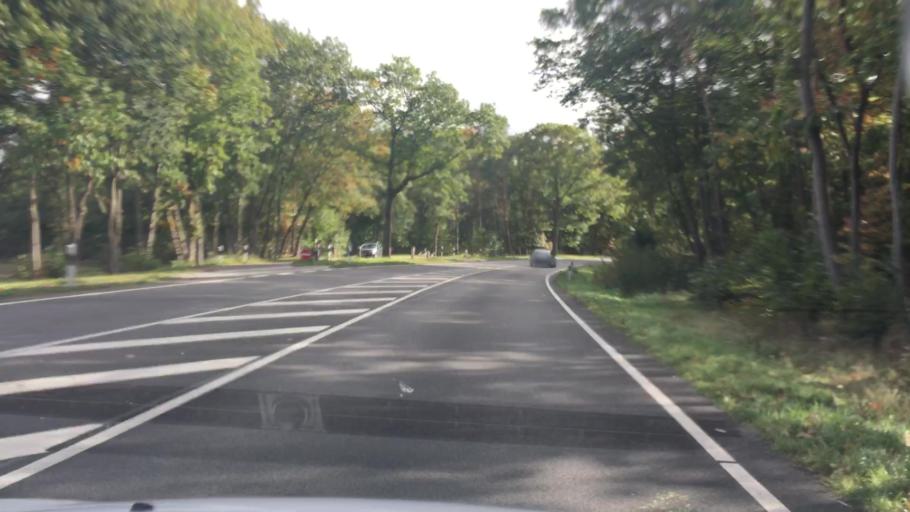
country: DE
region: Lower Saxony
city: Diepholz
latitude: 52.6547
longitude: 8.3354
